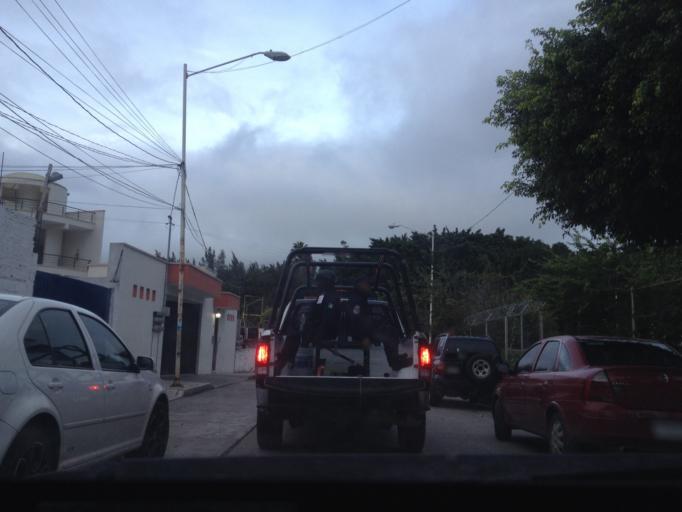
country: MX
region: Guerrero
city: Chilpancingo de los Bravos
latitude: 17.5474
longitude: -99.5020
